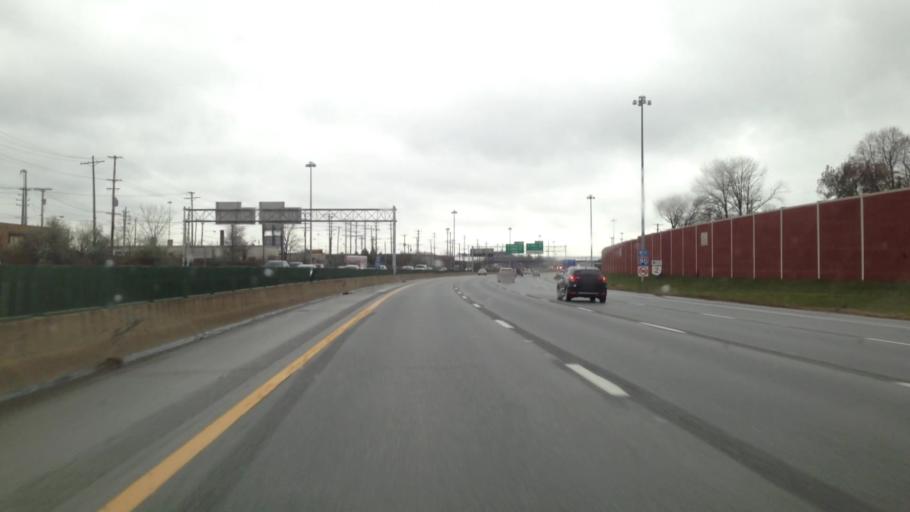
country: US
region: Ohio
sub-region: Cuyahoga County
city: Euclid
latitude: 41.5742
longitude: -81.5571
